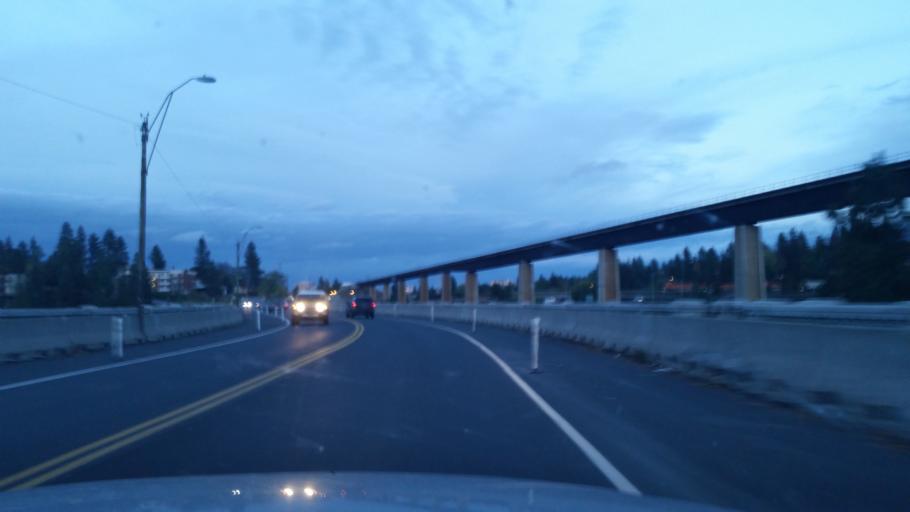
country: US
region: Washington
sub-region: Spokane County
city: Spokane
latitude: 47.6492
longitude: -117.4497
